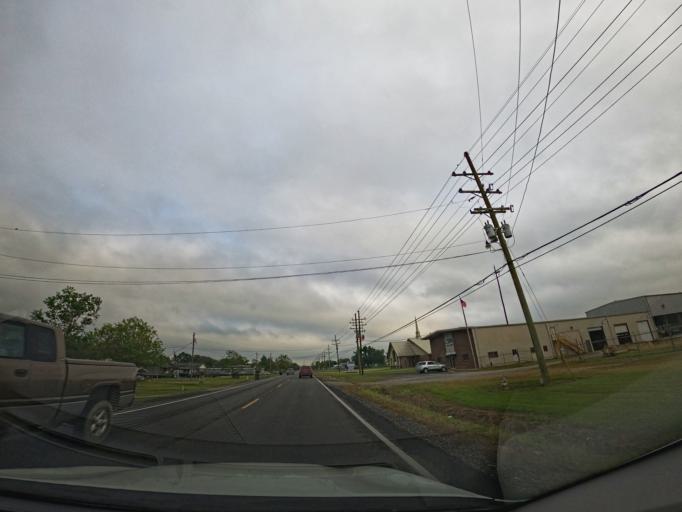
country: US
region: Louisiana
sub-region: Terrebonne Parish
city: Presquille
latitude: 29.5116
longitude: -90.6756
